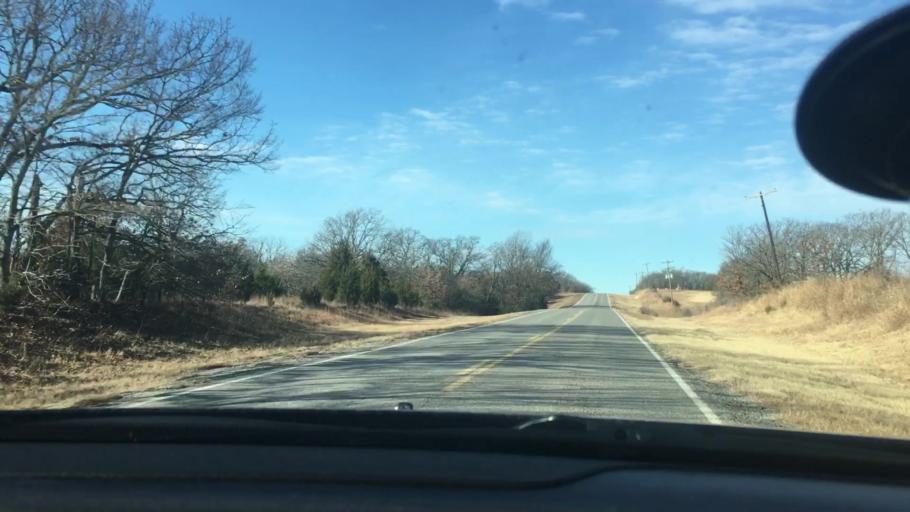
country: US
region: Oklahoma
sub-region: Seminole County
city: Konawa
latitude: 34.9857
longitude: -96.8702
